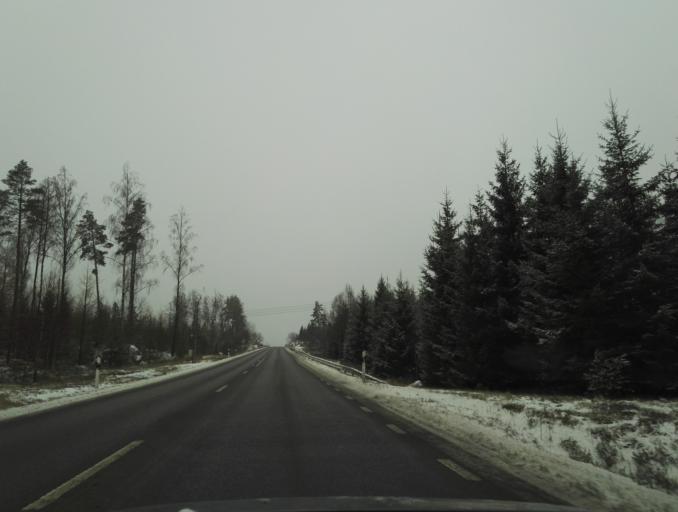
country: SE
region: Kronoberg
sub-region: Vaxjo Kommun
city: Gemla
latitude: 56.8265
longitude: 14.6919
